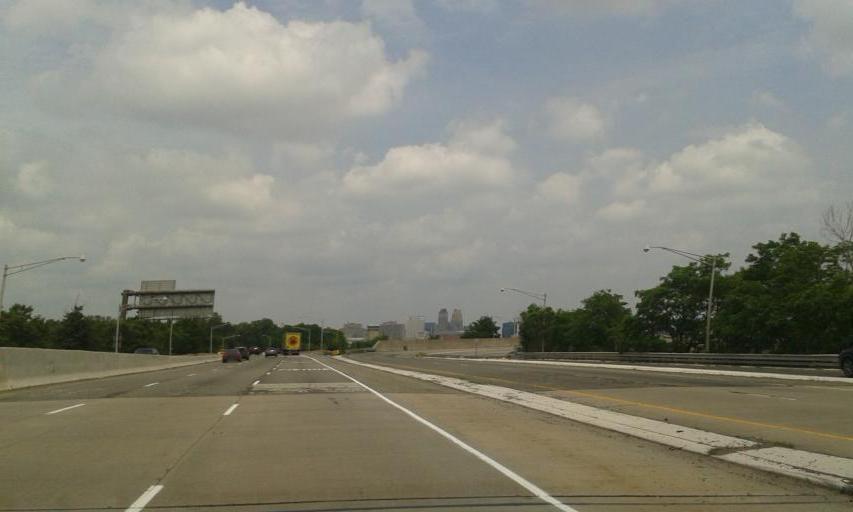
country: US
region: New Jersey
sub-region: Essex County
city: Newark
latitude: 40.7088
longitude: -74.1776
